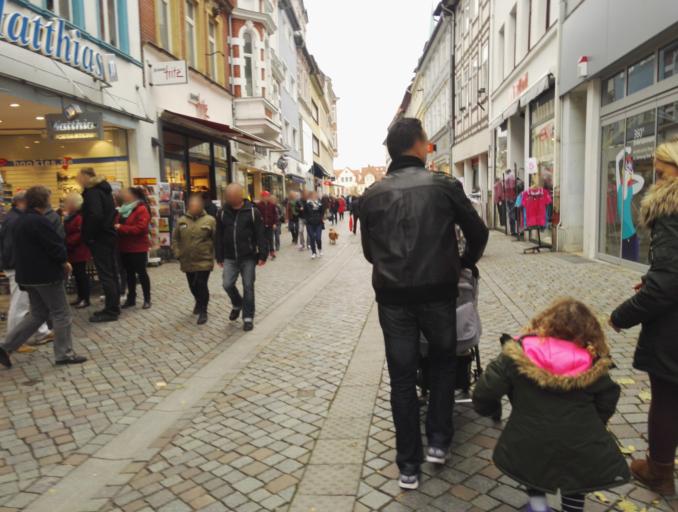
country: DE
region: Lower Saxony
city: Hameln
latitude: 52.1034
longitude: 9.3563
